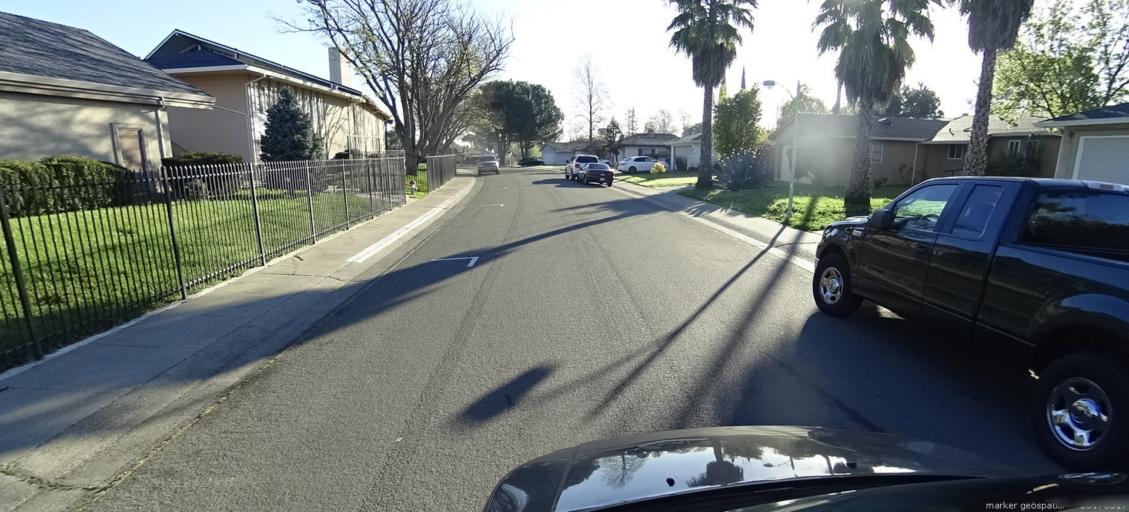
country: US
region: California
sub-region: Sacramento County
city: Parkway
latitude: 38.4942
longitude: -121.4971
